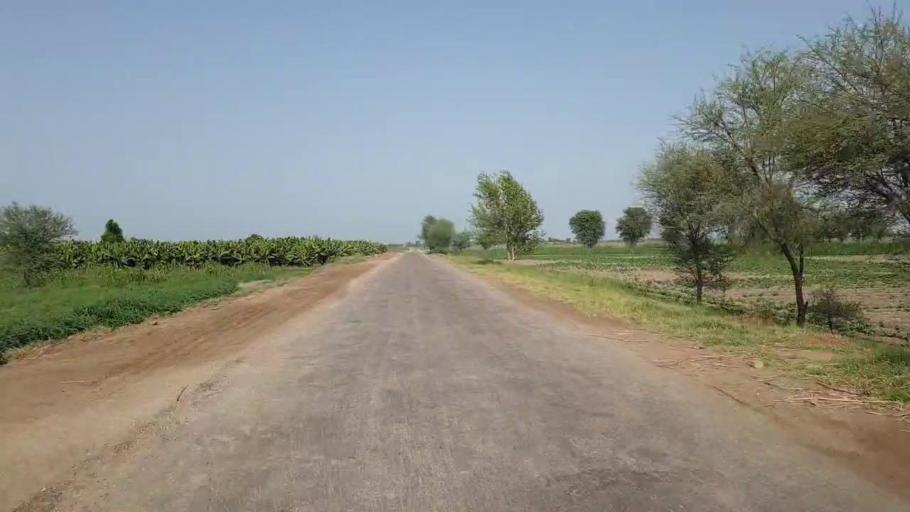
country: PK
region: Sindh
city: Sakrand
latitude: 26.2846
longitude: 68.2364
